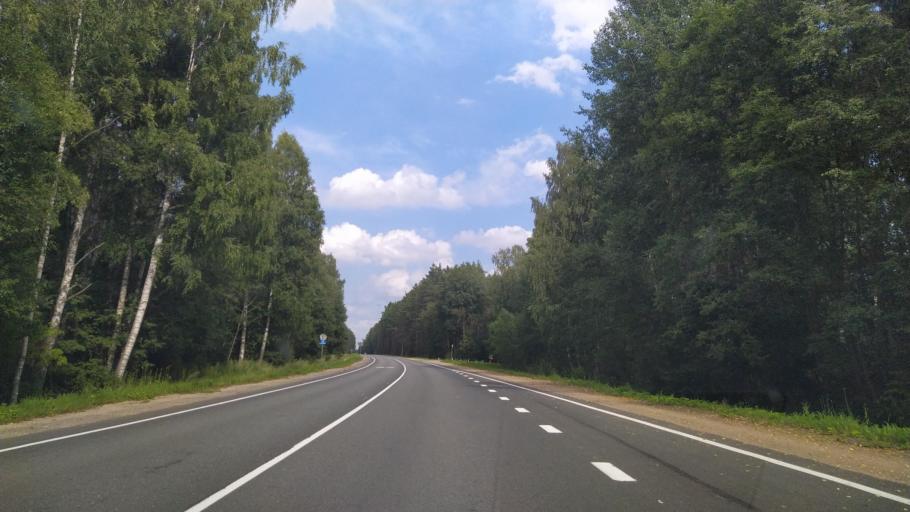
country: RU
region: Pskov
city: Dno
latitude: 57.9831
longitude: 29.7938
